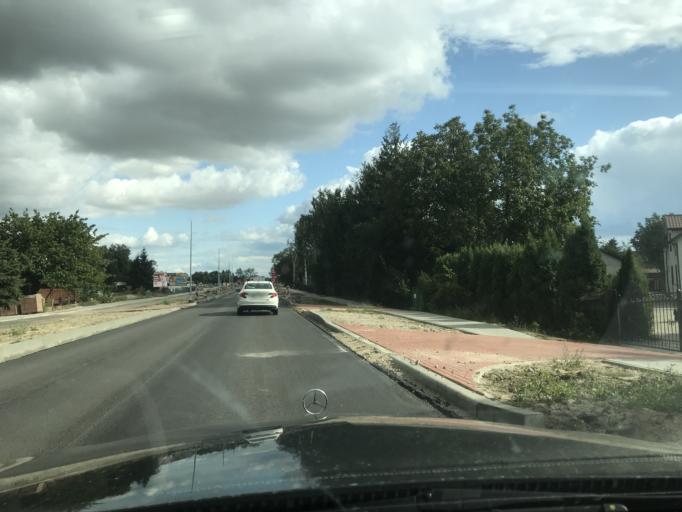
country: PL
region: Lublin Voivodeship
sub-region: Powiat lubartowski
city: Lubartow
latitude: 51.4755
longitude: 22.6013
